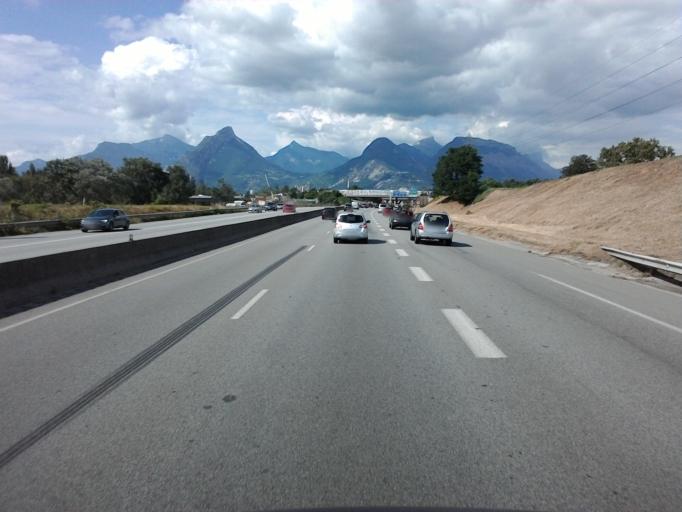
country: FR
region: Rhone-Alpes
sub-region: Departement de l'Isere
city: Seyssins
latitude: 45.1548
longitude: 5.6990
